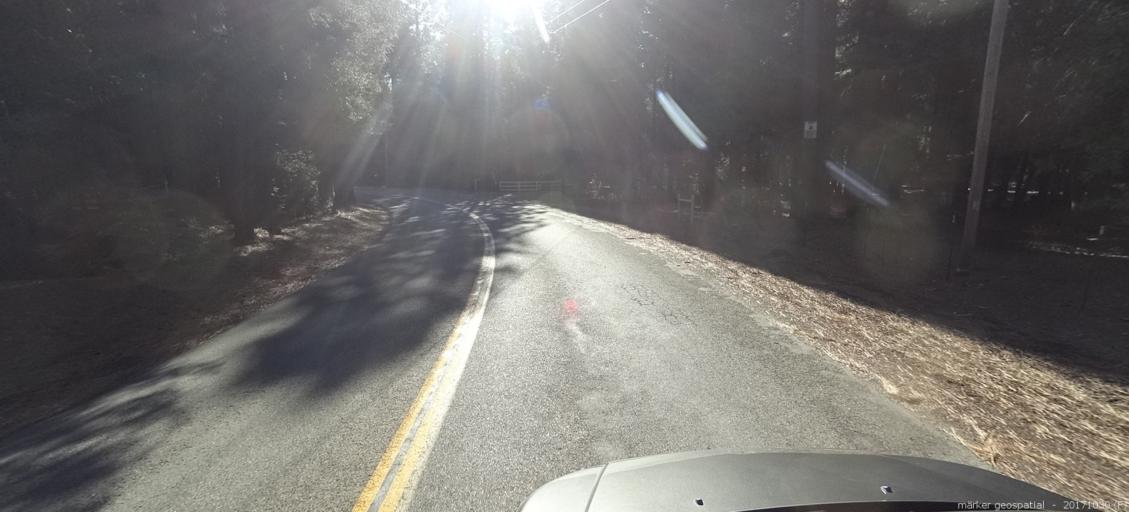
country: US
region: California
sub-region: Shasta County
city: Shingletown
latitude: 40.5237
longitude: -121.7496
